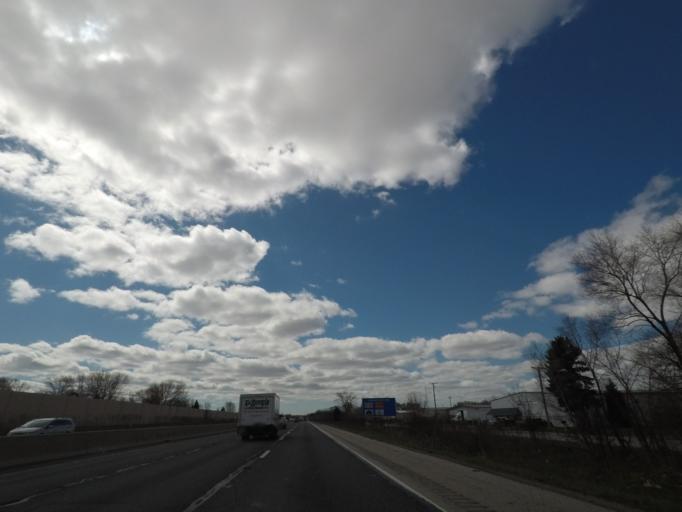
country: US
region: Illinois
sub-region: Will County
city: Crystal Lawns
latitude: 41.5471
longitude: -88.1803
